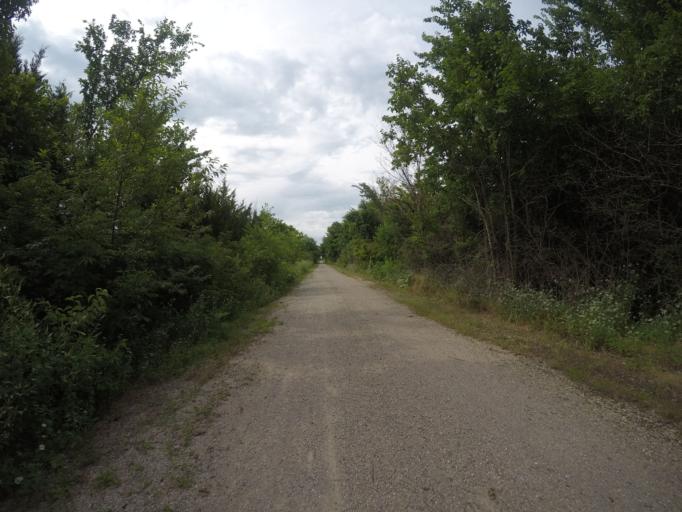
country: US
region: Kansas
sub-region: Anderson County
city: Garnett
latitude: 38.4376
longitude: -95.2641
